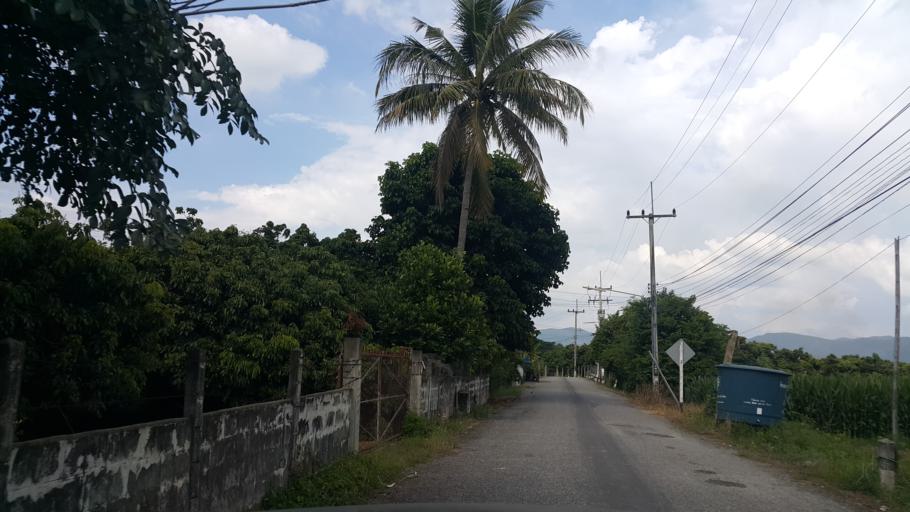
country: TH
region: Chiang Mai
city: San Sai
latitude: 18.8924
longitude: 99.1206
